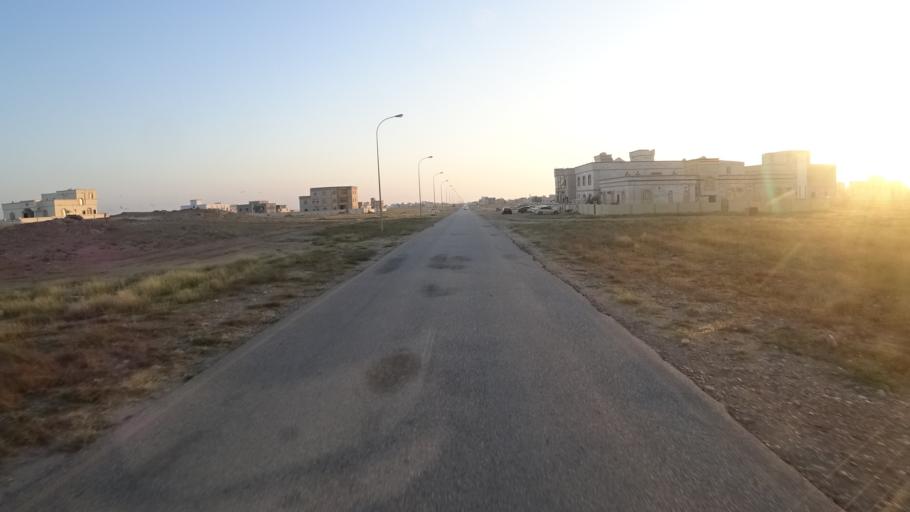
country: OM
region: Zufar
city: Salalah
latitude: 16.9928
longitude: 54.7188
